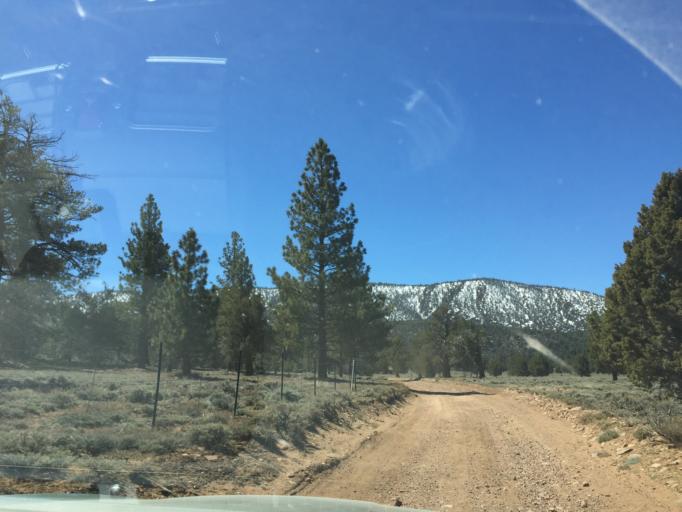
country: US
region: California
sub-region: San Bernardino County
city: Big Bear City
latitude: 34.2276
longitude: -116.7222
